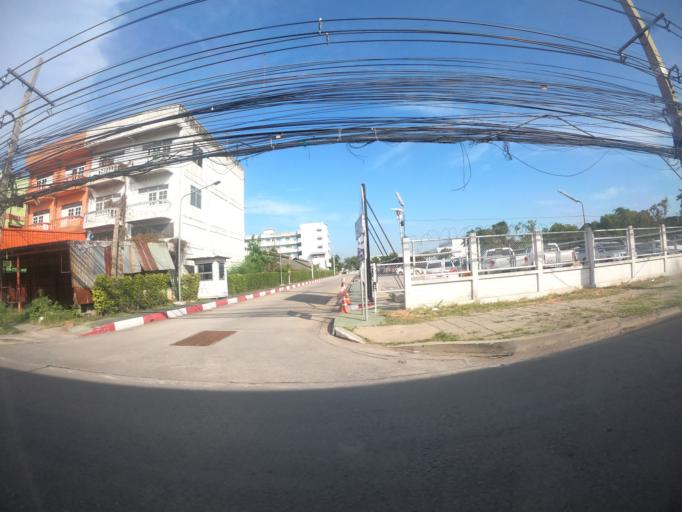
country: TH
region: Phra Nakhon Si Ayutthaya
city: Wang Noi
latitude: 14.2291
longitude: 100.7098
